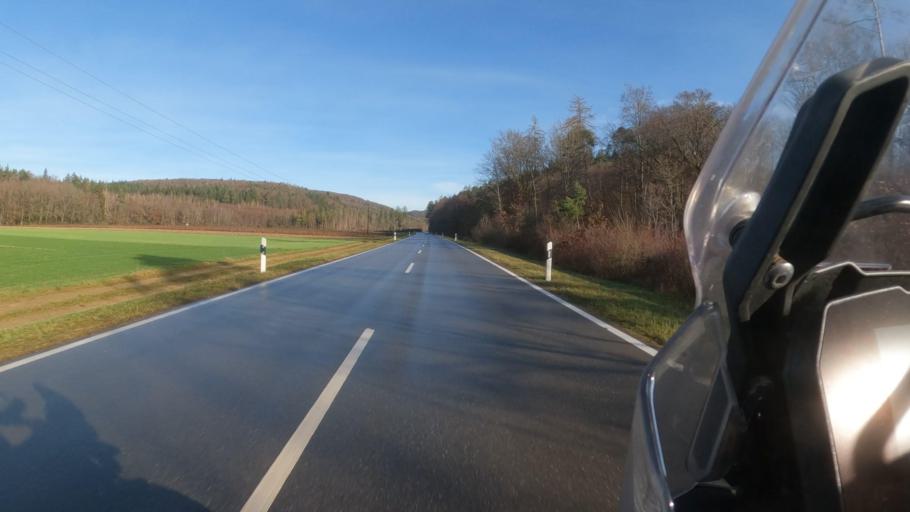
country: DE
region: Baden-Wuerttemberg
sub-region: Freiburg Region
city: Muhlhausen-Ehingen
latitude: 47.8424
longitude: 8.8179
